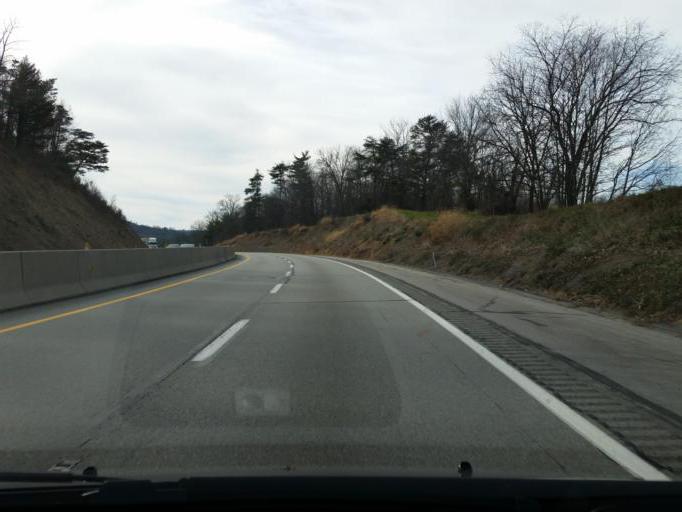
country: US
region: Pennsylvania
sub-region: Fulton County
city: McConnellsburg
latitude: 40.0586
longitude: -77.9529
